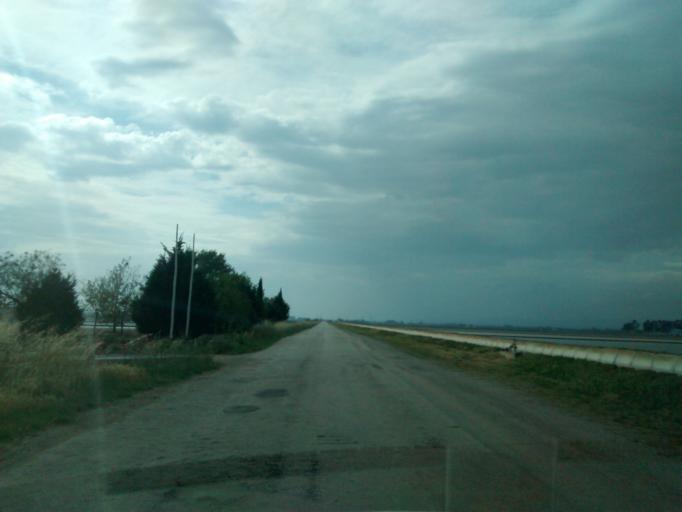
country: ES
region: Catalonia
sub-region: Provincia de Tarragona
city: Deltebre
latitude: 40.6935
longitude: 0.7703
